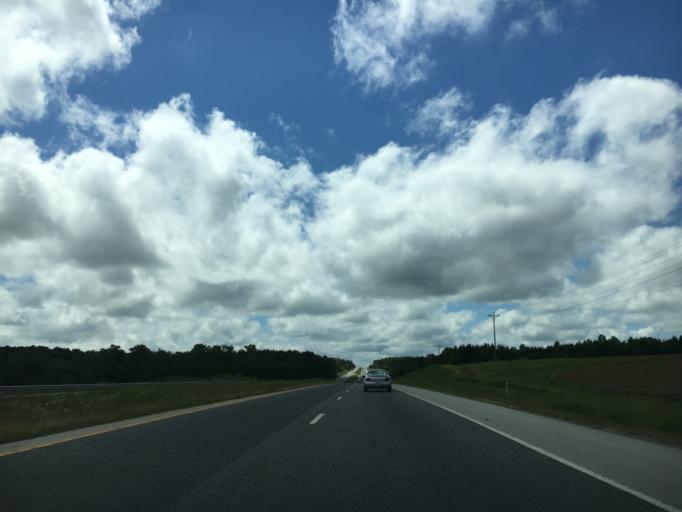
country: US
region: Virginia
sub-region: Mecklenburg County
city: Bracey
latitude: 36.6713
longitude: -78.2379
